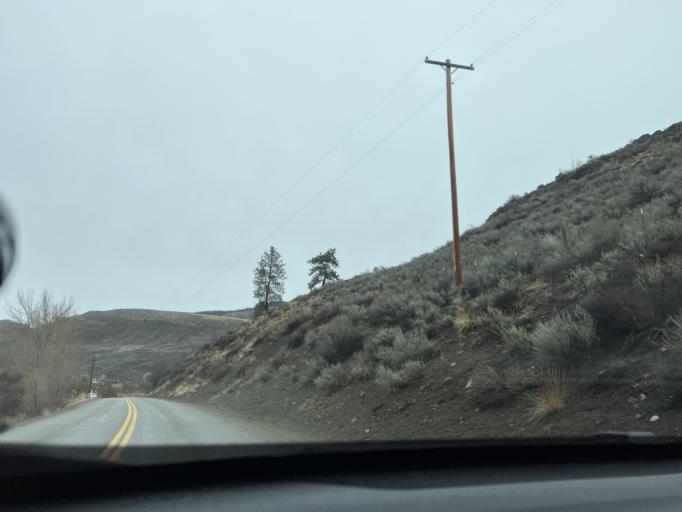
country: US
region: Washington
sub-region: Okanogan County
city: Brewster
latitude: 48.5079
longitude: -120.1734
